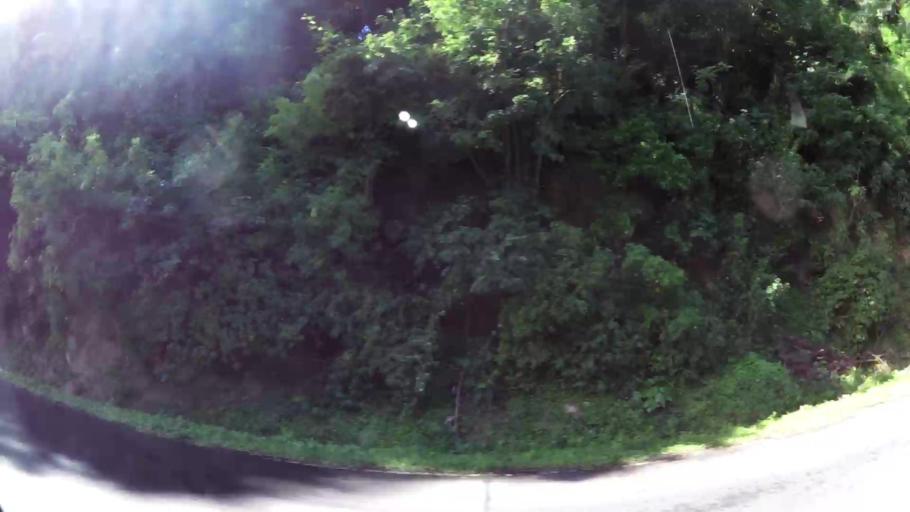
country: LC
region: Soufriere
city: Soufriere
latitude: 13.8345
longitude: -61.0537
